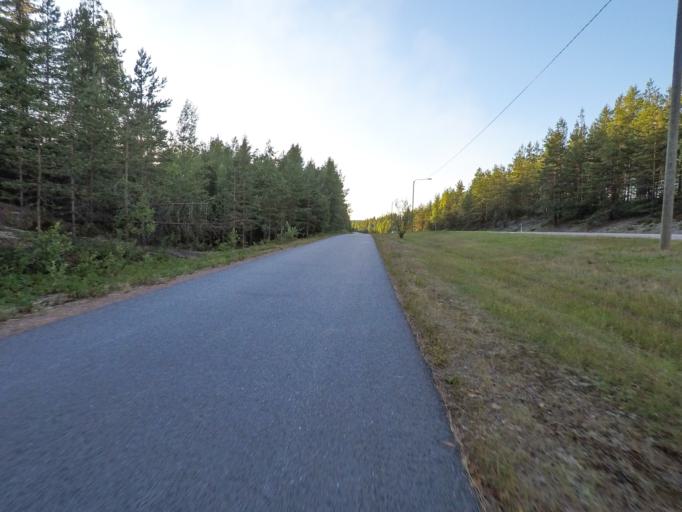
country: FI
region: South Karelia
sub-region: Imatra
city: Ruokolahti
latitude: 61.2635
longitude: 28.8793
